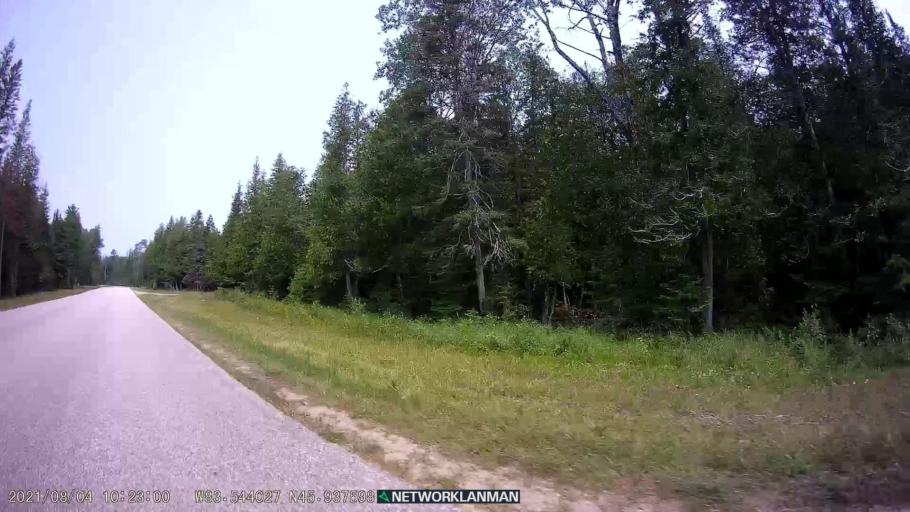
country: CA
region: Ontario
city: Thessalon
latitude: 45.9379
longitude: -83.5442
